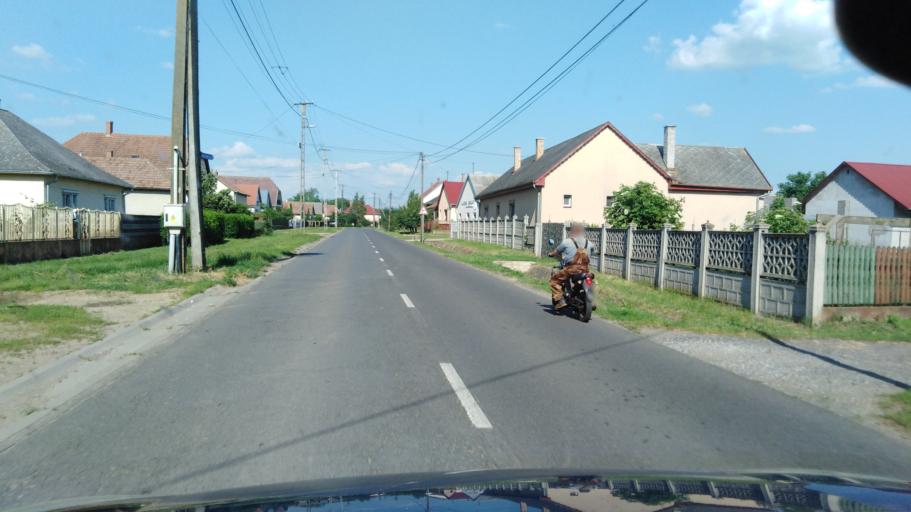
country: HU
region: Szabolcs-Szatmar-Bereg
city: Nyirvasvari
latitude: 47.8263
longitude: 22.1761
